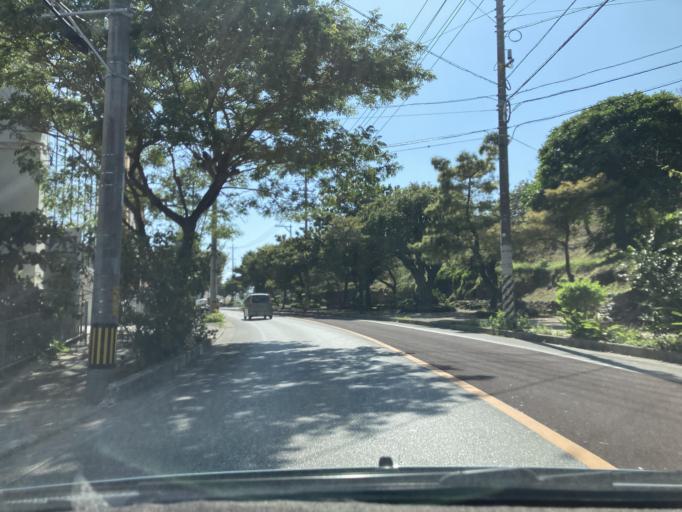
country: JP
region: Okinawa
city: Ginowan
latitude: 26.2590
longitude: 127.7232
